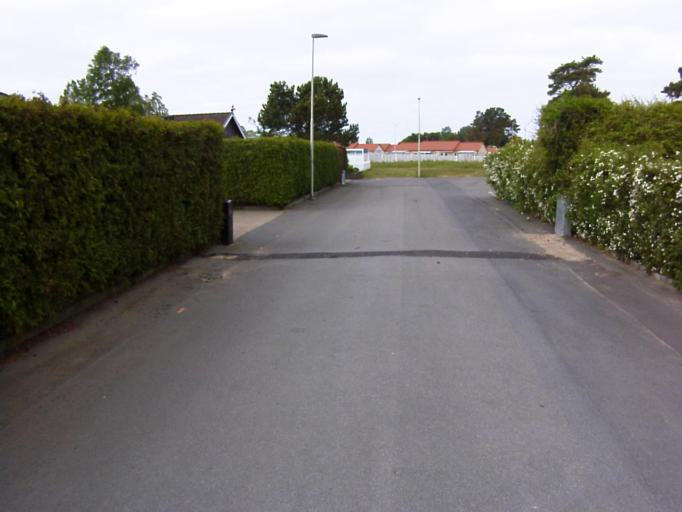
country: SE
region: Skane
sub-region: Kristianstads Kommun
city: Ahus
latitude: 55.9359
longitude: 14.2927
